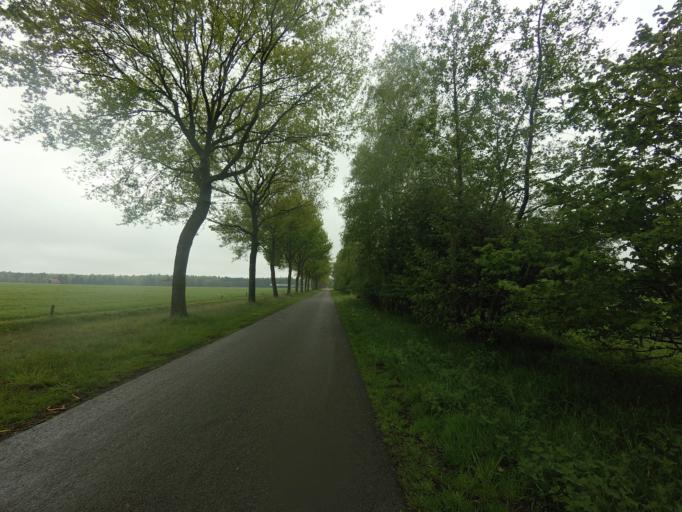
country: DE
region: North Rhine-Westphalia
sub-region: Regierungsbezirk Munster
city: Vreden
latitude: 52.1245
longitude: 6.8292
